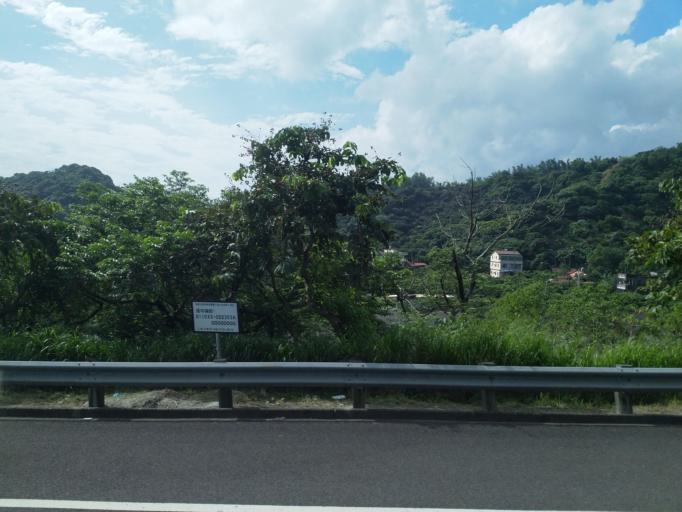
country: TW
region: Taiwan
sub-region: Pingtung
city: Pingtung
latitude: 22.7966
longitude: 120.4471
